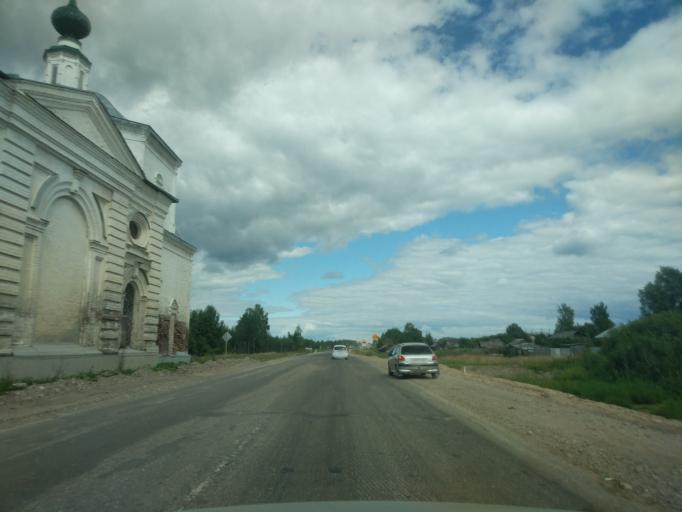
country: RU
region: Kostroma
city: Sudislavl'
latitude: 57.8625
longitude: 41.6204
